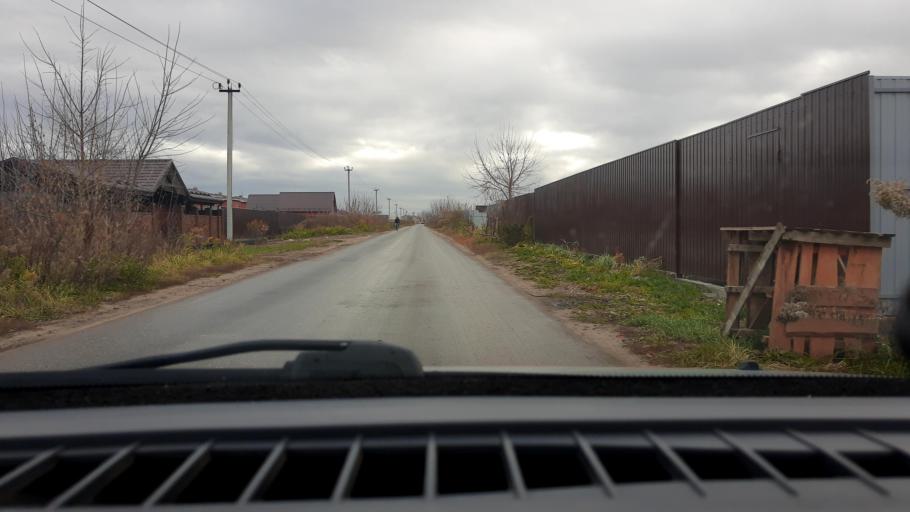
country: RU
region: Nizjnij Novgorod
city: Afonino
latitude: 56.2051
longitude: 44.1281
